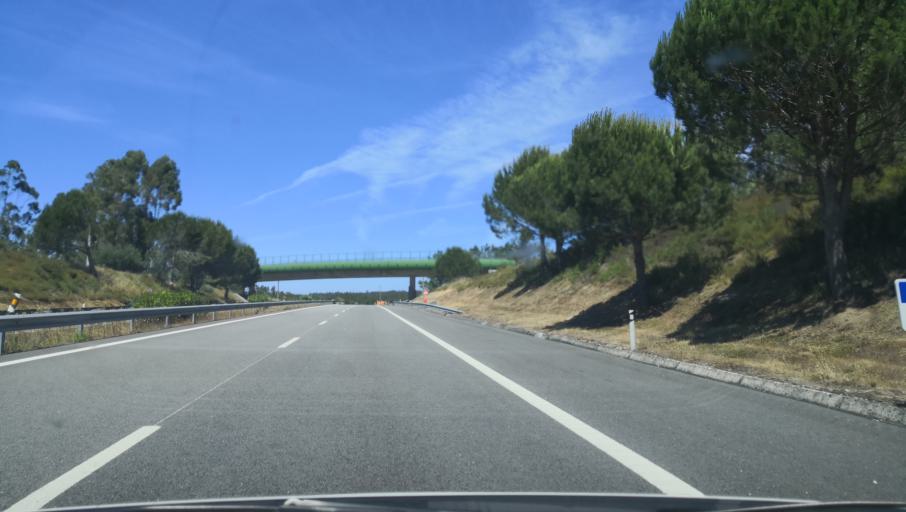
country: PT
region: Coimbra
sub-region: Montemor-O-Velho
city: Arazede
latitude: 40.2315
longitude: -8.6663
